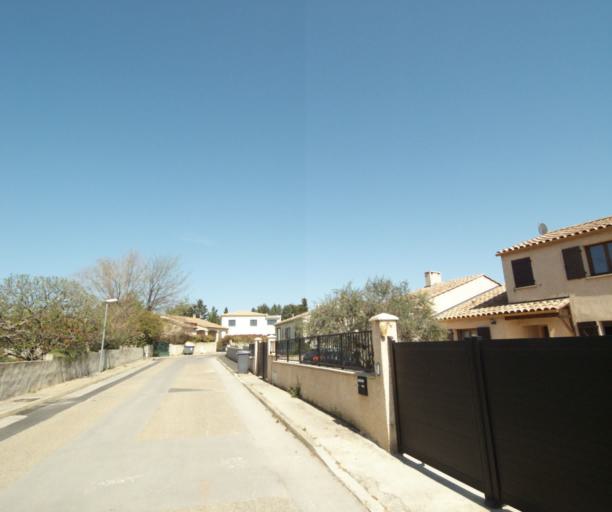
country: FR
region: Languedoc-Roussillon
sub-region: Departement de l'Herault
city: Sussargues
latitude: 43.7102
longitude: 3.9985
